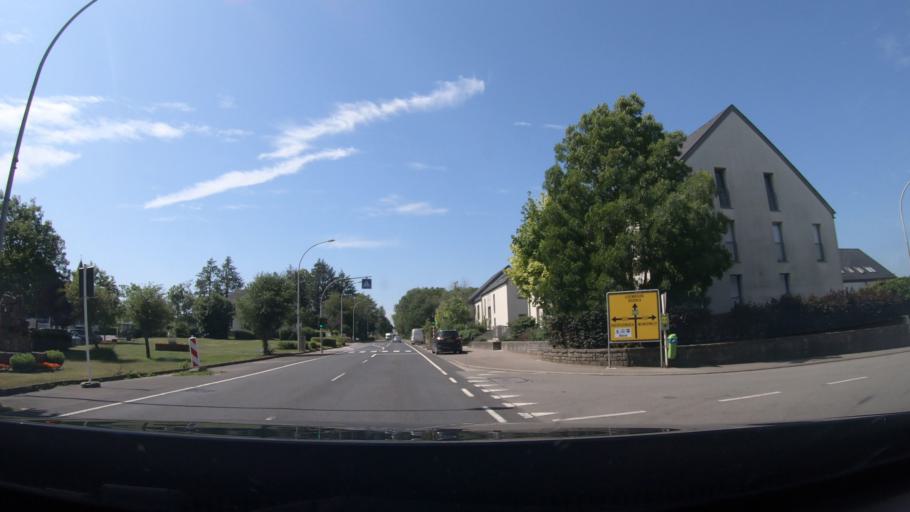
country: LU
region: Diekirch
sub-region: Canton de Clervaux
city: Hosingen
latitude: 50.0133
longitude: 6.0903
